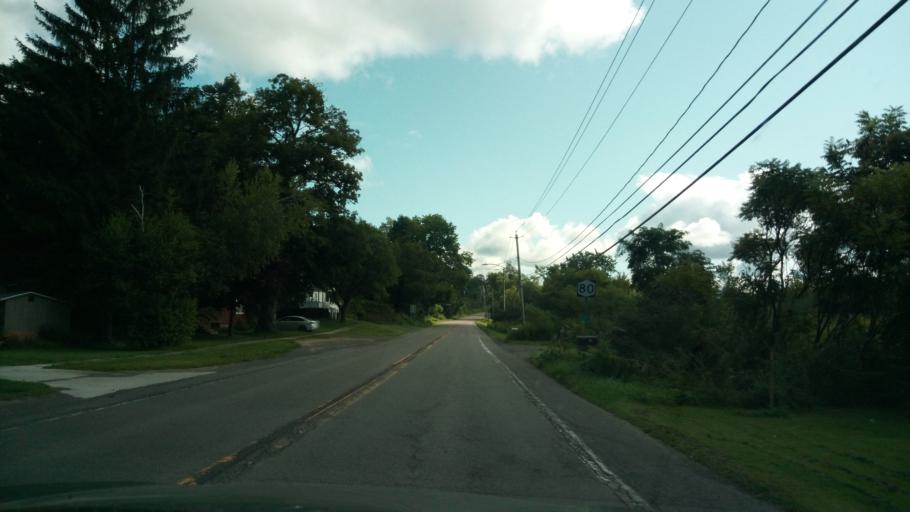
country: US
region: New York
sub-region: Onondaga County
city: Nedrow
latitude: 42.8001
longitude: -76.1037
